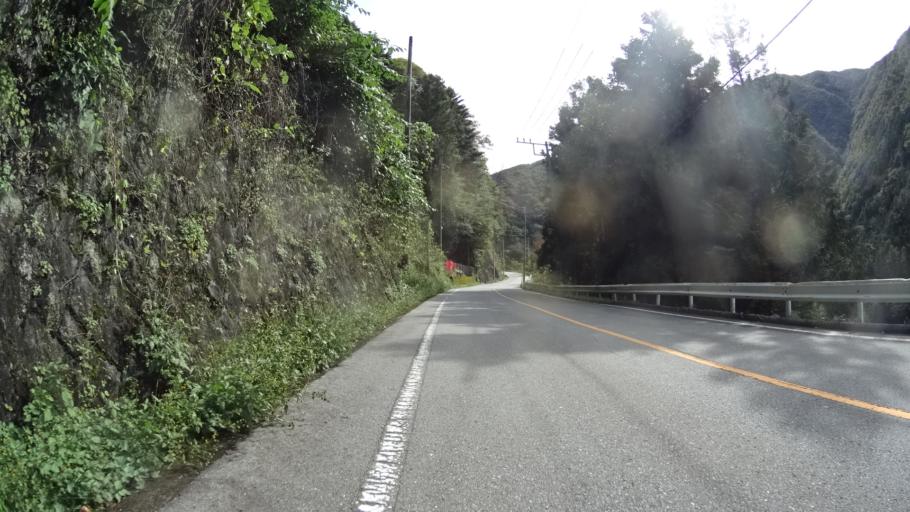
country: JP
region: Yamanashi
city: Otsuki
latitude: 35.7876
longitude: 138.9455
